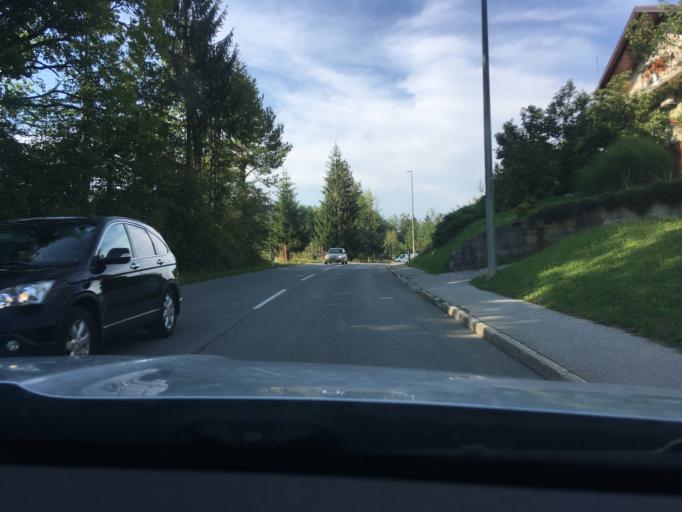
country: SI
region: Crnomelj
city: Crnomelj
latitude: 45.5635
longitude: 15.1722
